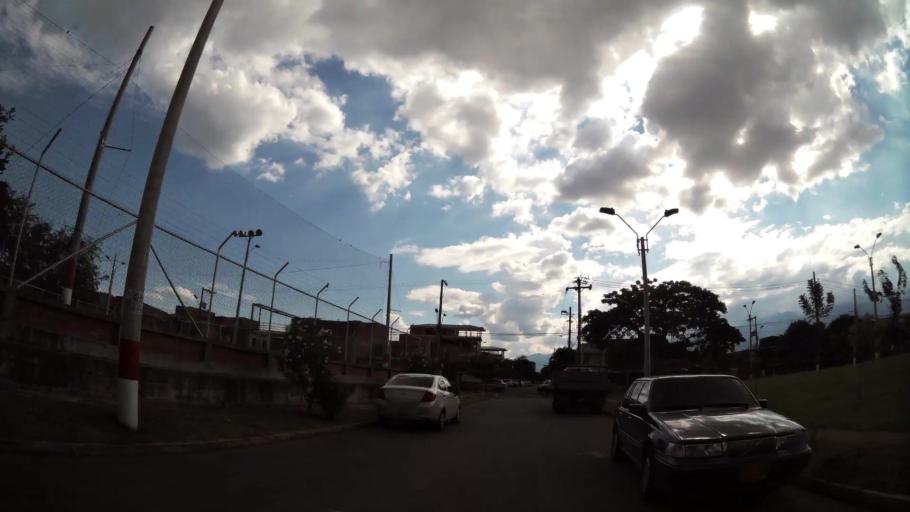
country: CO
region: Valle del Cauca
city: Cali
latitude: 3.4032
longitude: -76.5003
